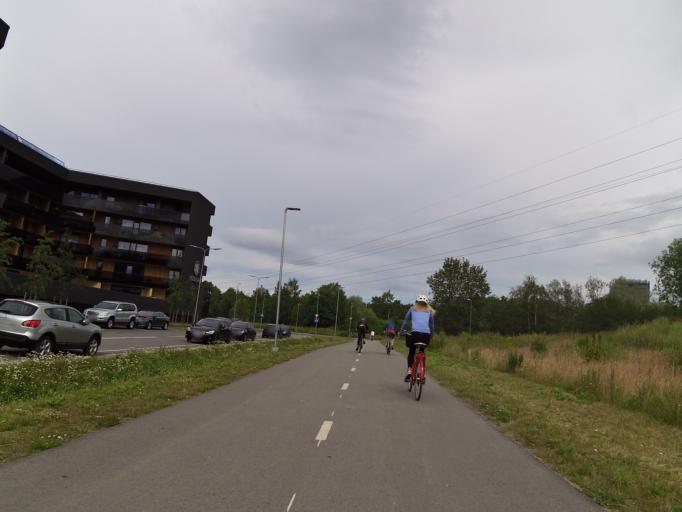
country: EE
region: Harju
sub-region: Tallinna linn
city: Tallinn
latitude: 59.4309
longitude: 24.6857
